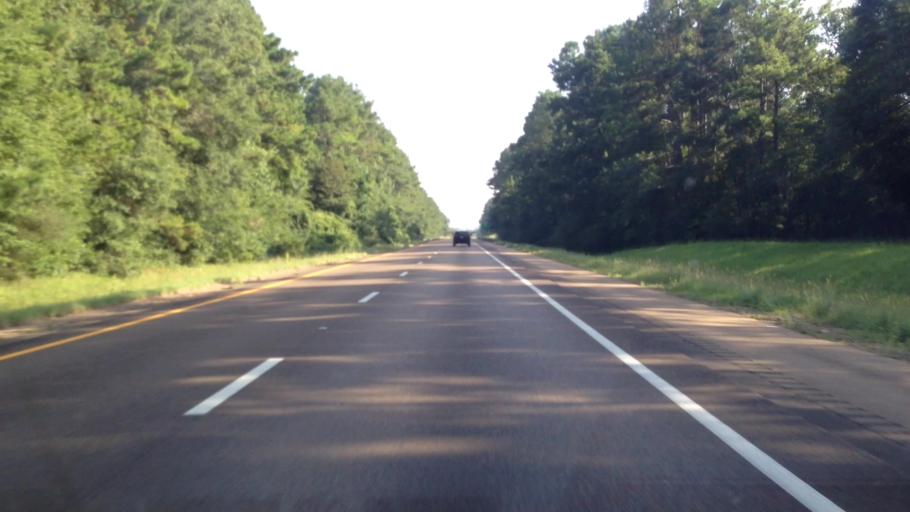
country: US
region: Mississippi
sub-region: Pike County
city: Summit
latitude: 31.3423
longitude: -90.4780
